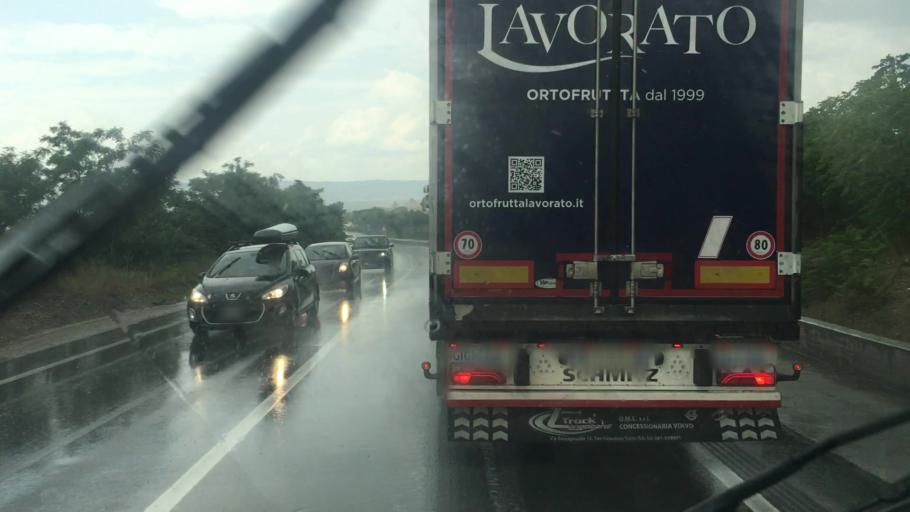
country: IT
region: Basilicate
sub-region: Provincia di Matera
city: Matera
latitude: 40.6286
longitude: 16.5910
